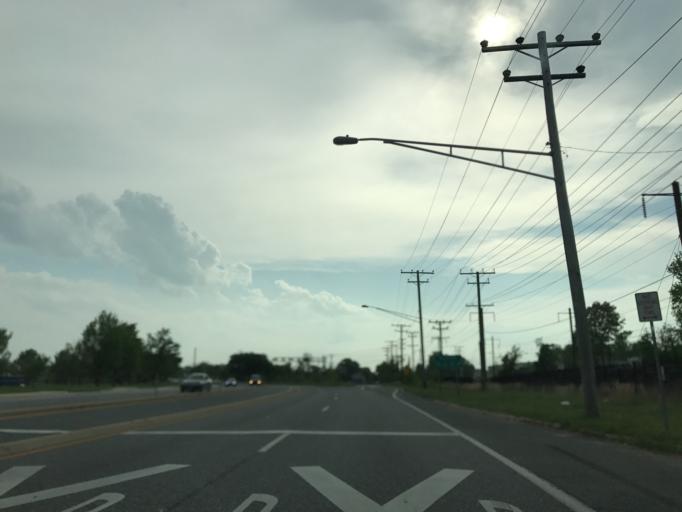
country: US
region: Maryland
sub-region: Baltimore County
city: Middle River
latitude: 39.3338
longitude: -76.4344
